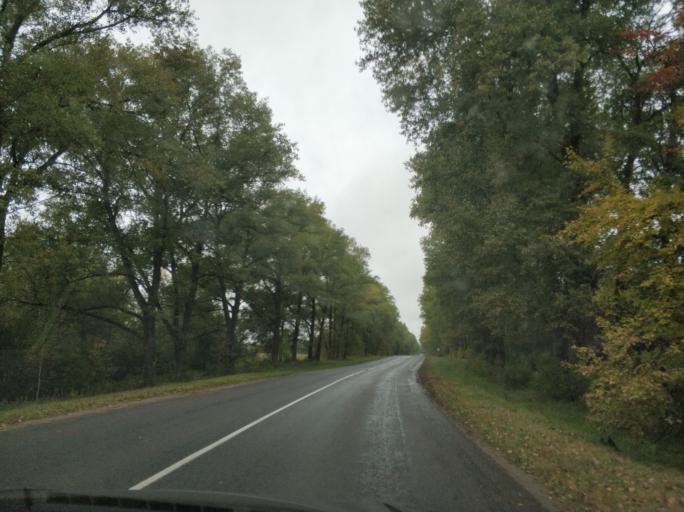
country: BY
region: Vitebsk
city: Polatsk
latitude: 55.4452
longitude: 28.9424
